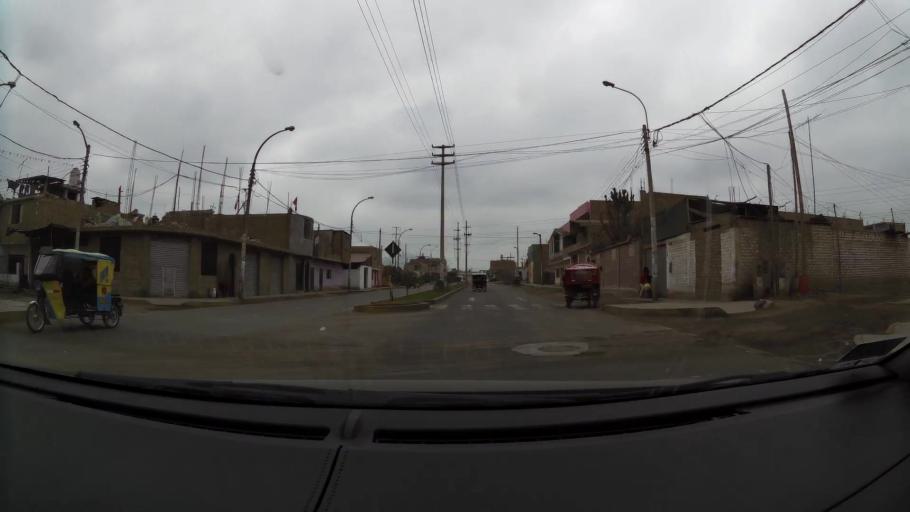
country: PE
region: Lima
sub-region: Provincia de Huaral
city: Huaral
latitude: -11.4994
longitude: -77.2008
